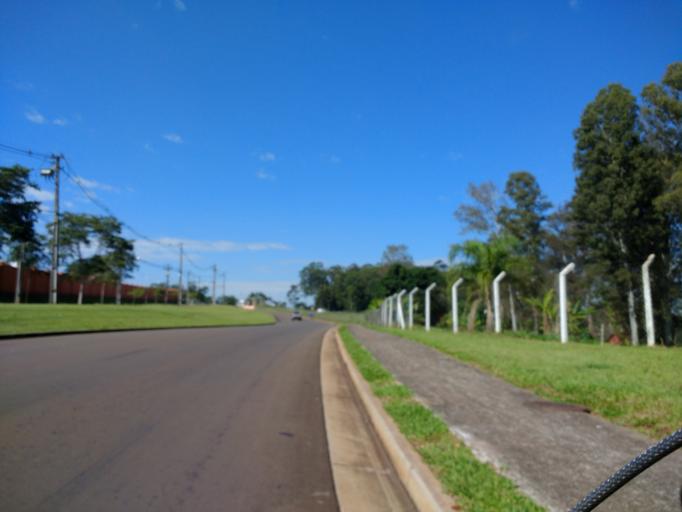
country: BR
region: Parana
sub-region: Londrina
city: Londrina
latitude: -23.3508
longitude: -51.1906
